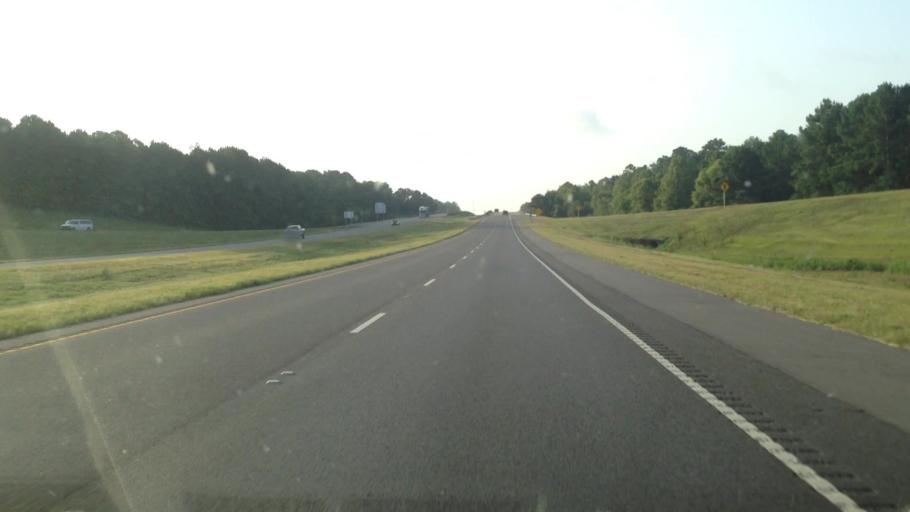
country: US
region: Louisiana
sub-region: Rapides Parish
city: Boyce
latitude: 31.4093
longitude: -92.7169
